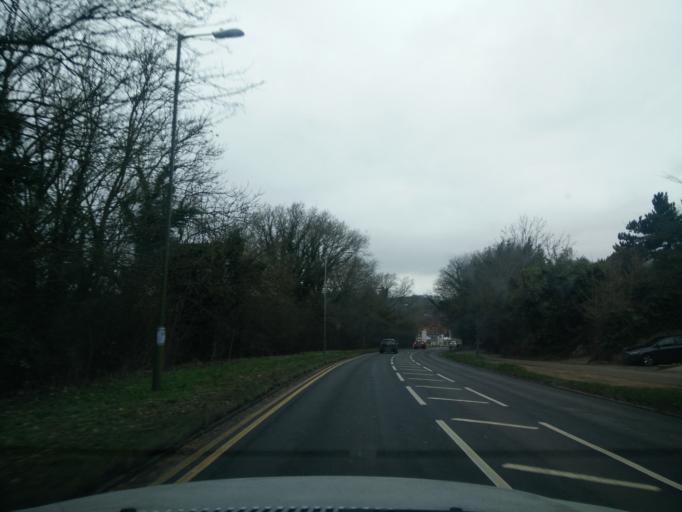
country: GB
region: England
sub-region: Buckinghamshire
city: Amersham on the Hill
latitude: 51.6640
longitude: -0.6040
